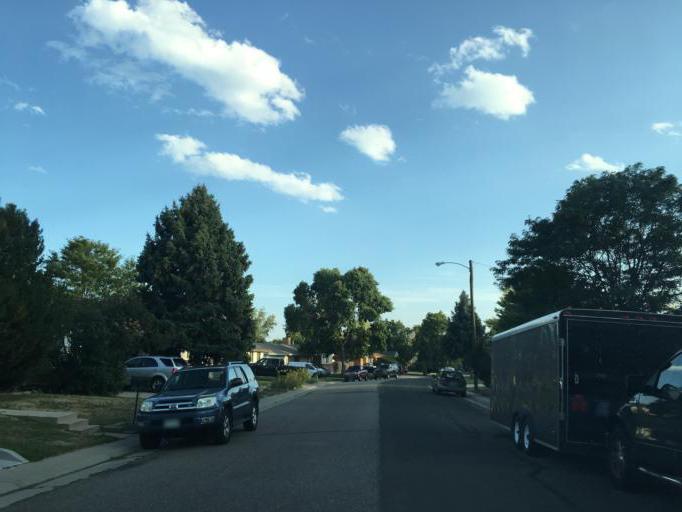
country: US
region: Colorado
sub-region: Jefferson County
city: Applewood
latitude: 39.7923
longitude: -105.1494
